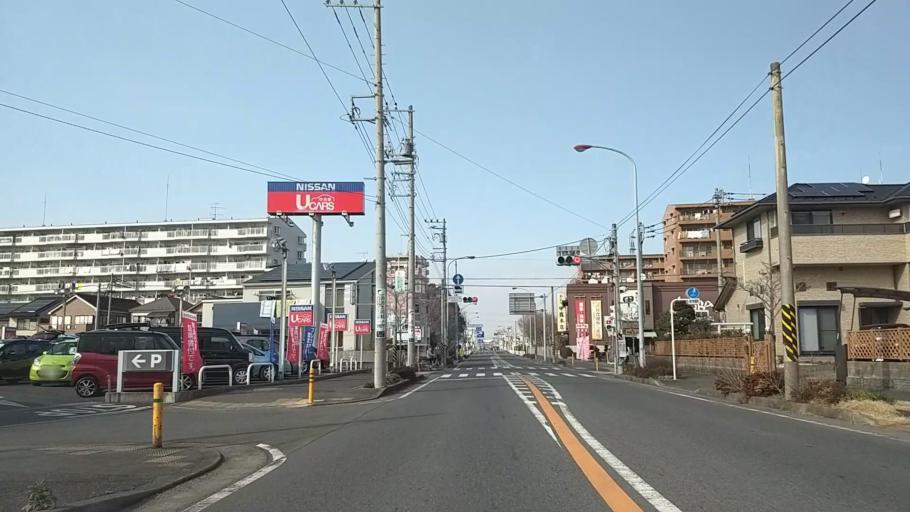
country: JP
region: Kanagawa
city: Chigasaki
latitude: 35.3384
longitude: 139.4137
